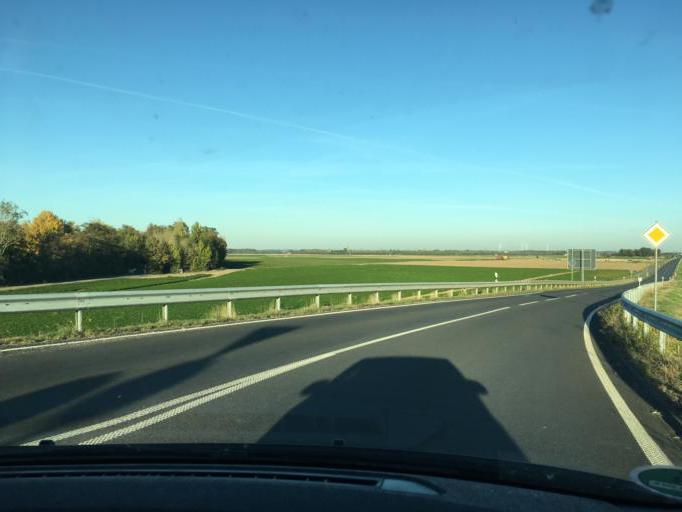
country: DE
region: North Rhine-Westphalia
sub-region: Regierungsbezirk Koln
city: Inden
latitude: 50.8359
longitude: 6.3843
